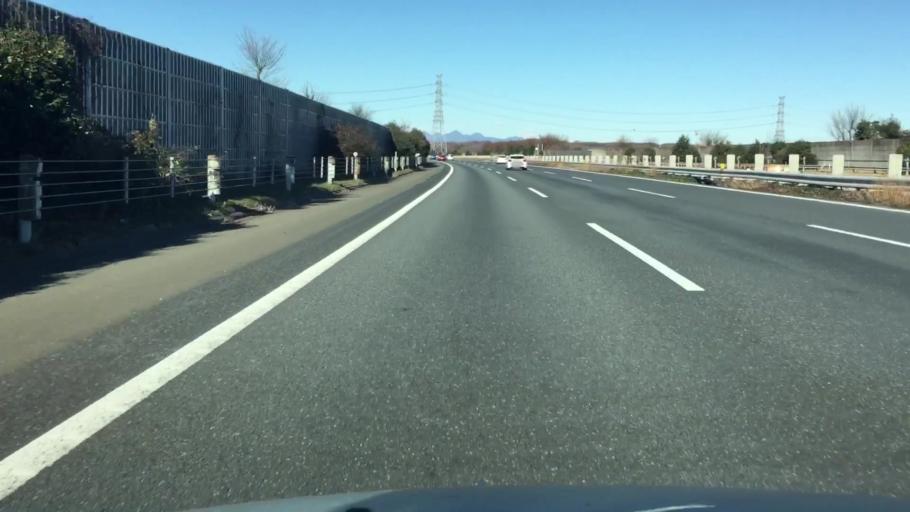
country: JP
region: Saitama
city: Honjo
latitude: 36.1977
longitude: 139.1849
